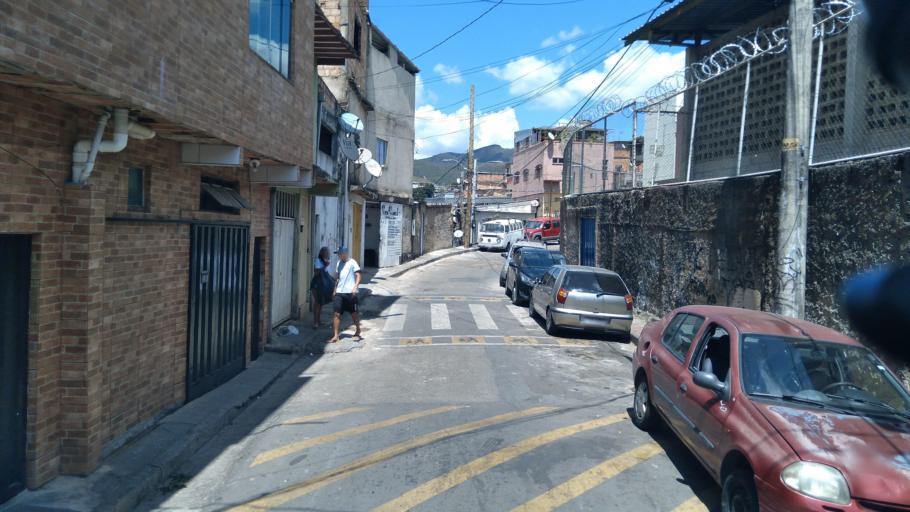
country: BR
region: Minas Gerais
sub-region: Belo Horizonte
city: Belo Horizonte
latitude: -19.9113
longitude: -43.8892
